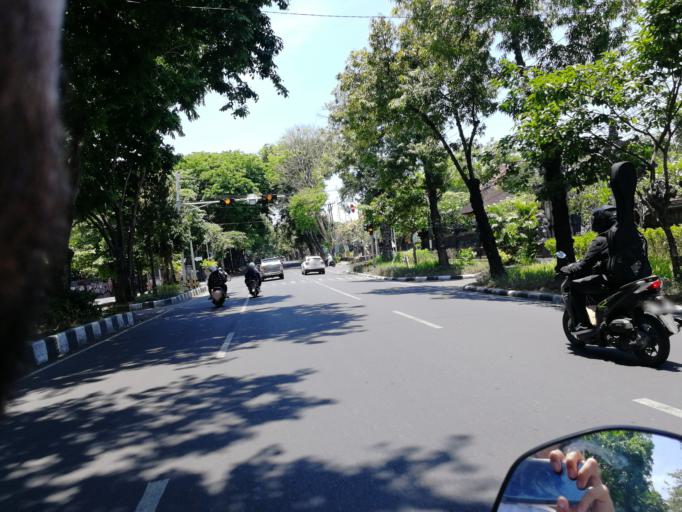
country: ID
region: Bali
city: Denpasar
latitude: -8.6671
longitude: 115.2299
